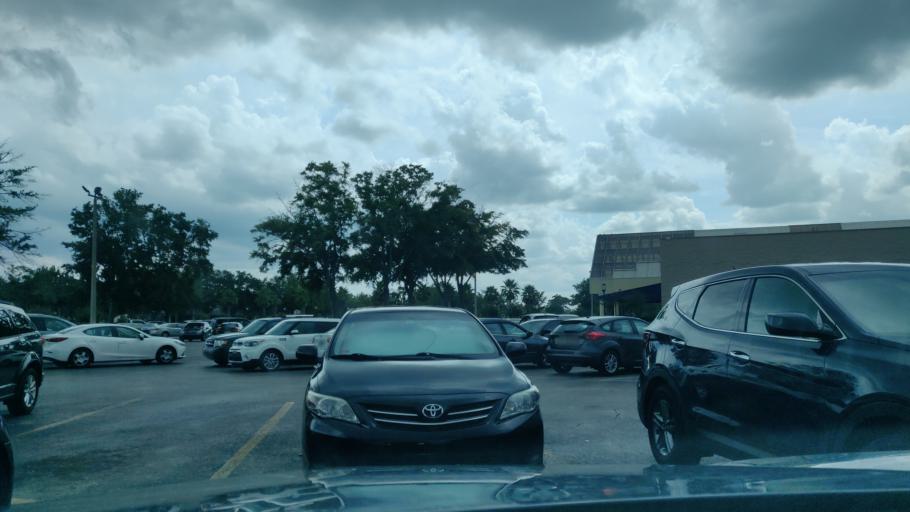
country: US
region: Florida
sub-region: Osceola County
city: Kissimmee
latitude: 28.3062
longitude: -81.4415
